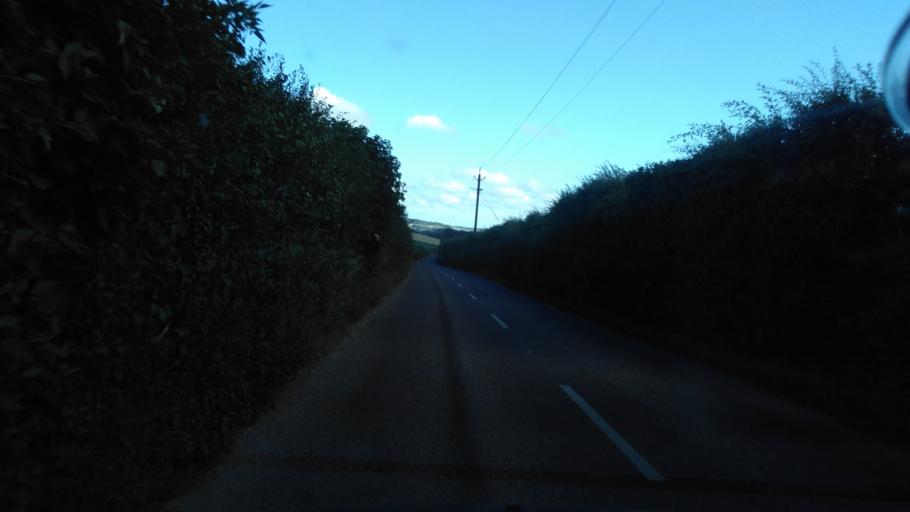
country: GB
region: England
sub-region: Kent
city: Dunkirk
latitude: 51.2601
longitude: 0.9543
